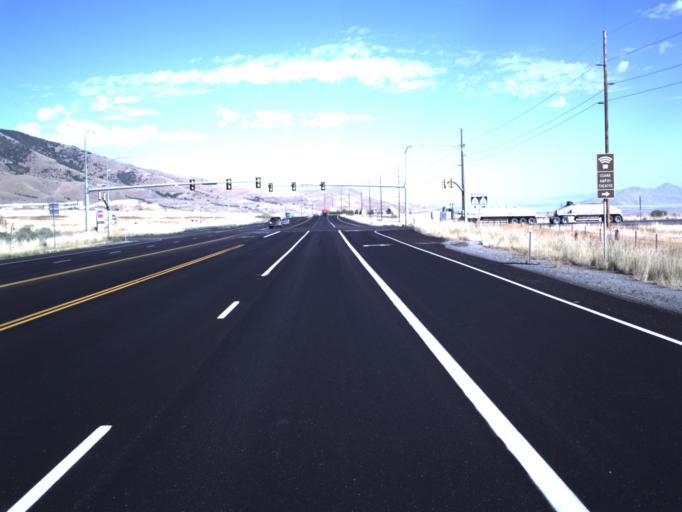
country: US
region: Utah
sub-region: Salt Lake County
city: Oquirrh
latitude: 40.6532
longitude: -112.0751
